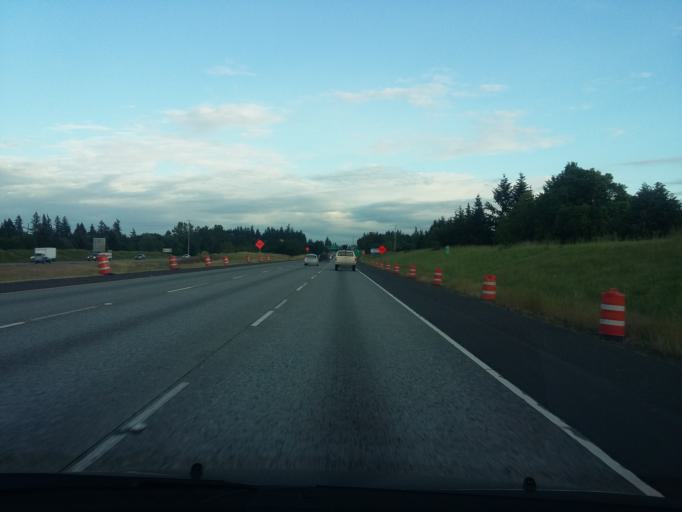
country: US
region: Washington
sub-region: Clark County
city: Orchards
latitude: 45.6451
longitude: -122.5651
